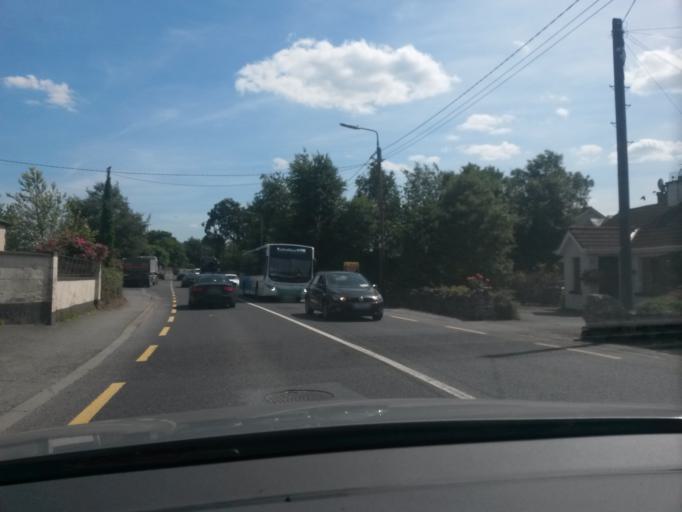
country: IE
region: Leinster
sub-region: Kildare
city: Sallins
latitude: 53.2573
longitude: -6.6684
